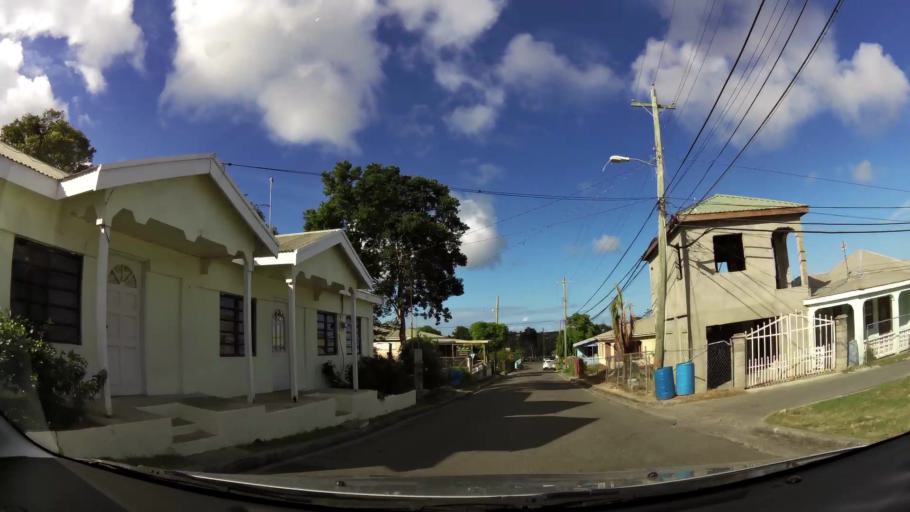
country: AG
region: Saint Peter
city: All Saints
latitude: 17.0649
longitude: -61.7946
